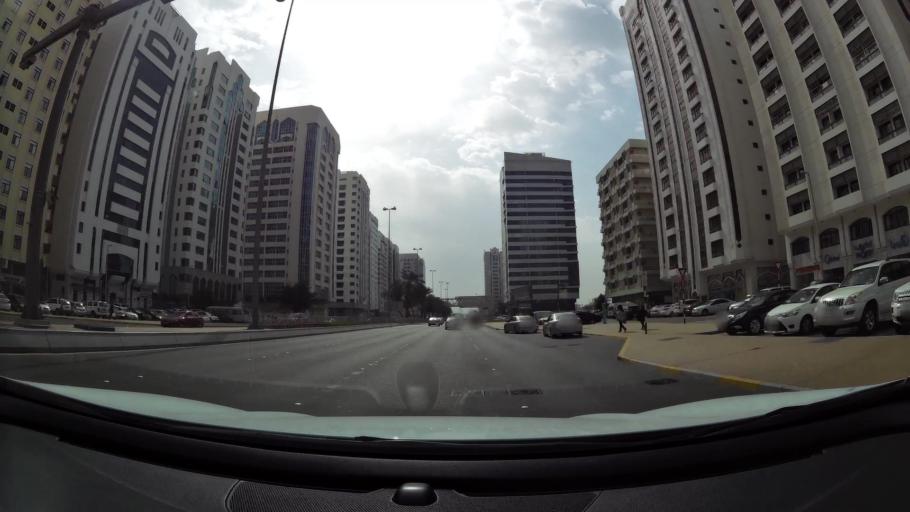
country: AE
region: Abu Dhabi
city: Abu Dhabi
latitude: 24.4616
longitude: 54.3786
